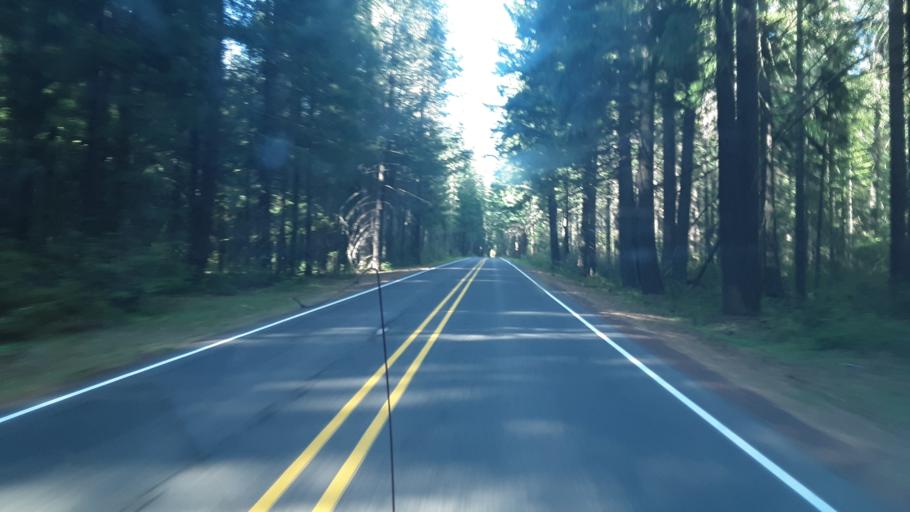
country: US
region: Oregon
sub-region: Jackson County
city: Shady Cove
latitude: 42.9320
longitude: -122.4221
